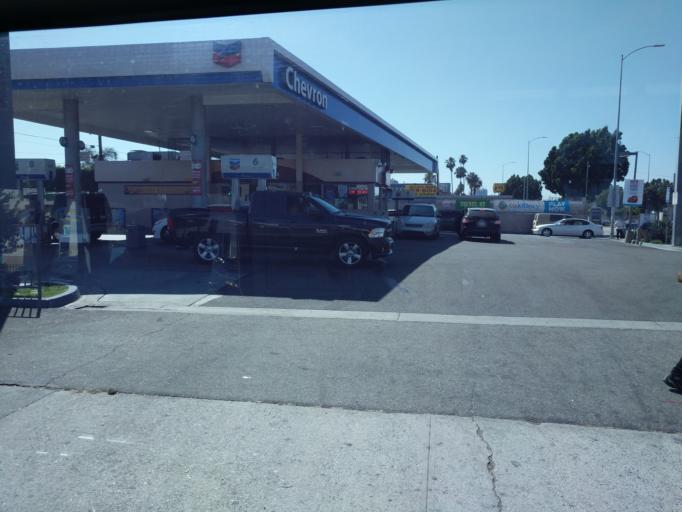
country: US
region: California
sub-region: Los Angeles County
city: Los Angeles
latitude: 34.0276
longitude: -118.2577
